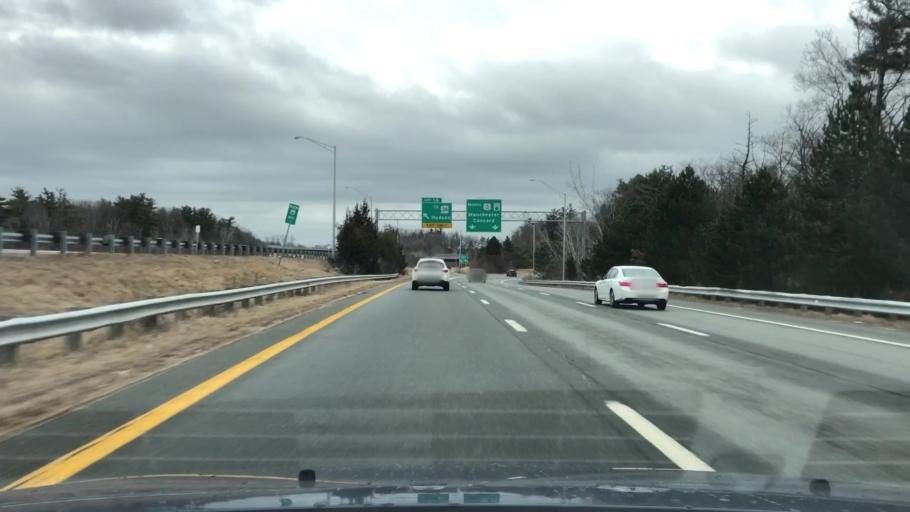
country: US
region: Massachusetts
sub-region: Middlesex County
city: Tyngsboro
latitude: 42.7141
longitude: -71.4495
